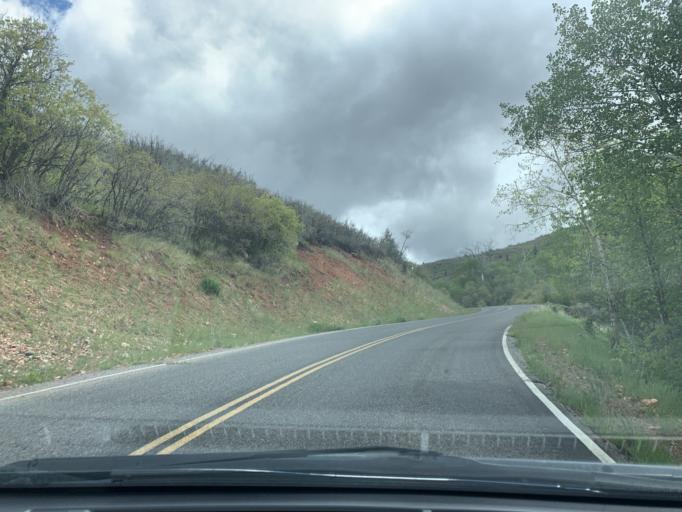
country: US
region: Utah
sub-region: Juab County
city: Nephi
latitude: 39.7764
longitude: -111.6998
